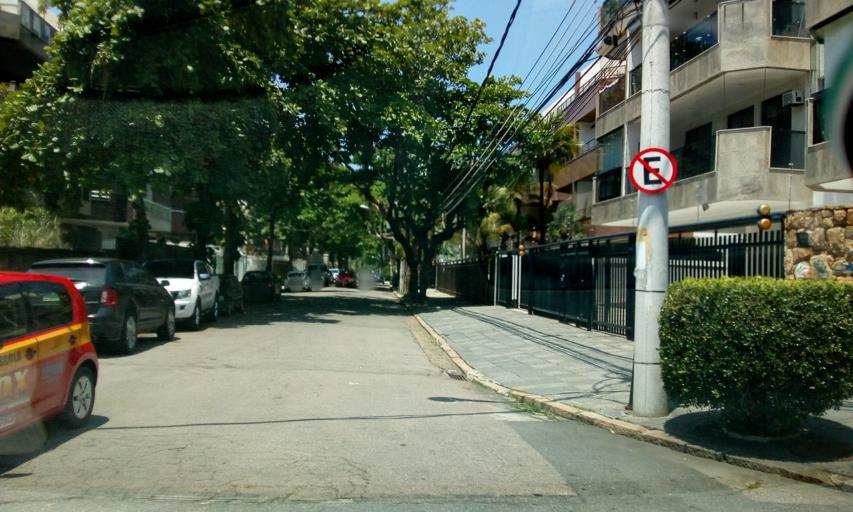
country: BR
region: Rio de Janeiro
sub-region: Nilopolis
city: Nilopolis
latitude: -23.0262
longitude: -43.4660
